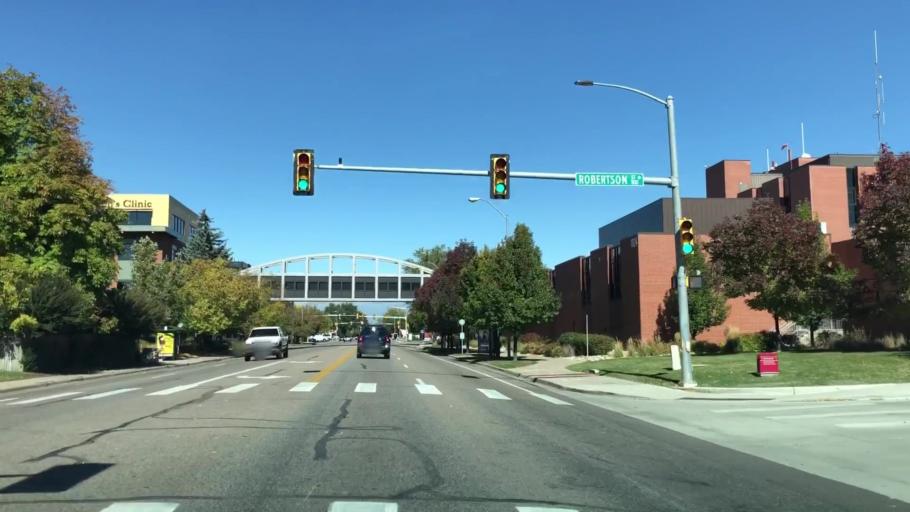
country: US
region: Colorado
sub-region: Larimer County
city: Fort Collins
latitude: 40.5711
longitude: -105.0579
